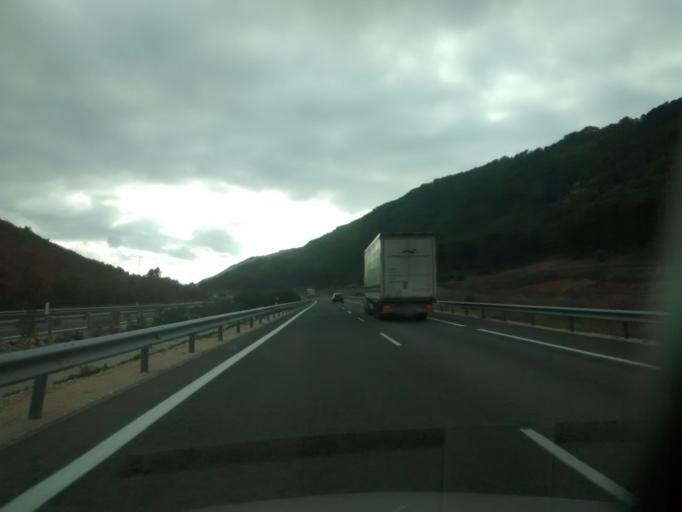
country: ES
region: Castille-La Mancha
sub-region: Provincia de Guadalajara
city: Ciruelas
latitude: 40.7141
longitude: -3.0685
